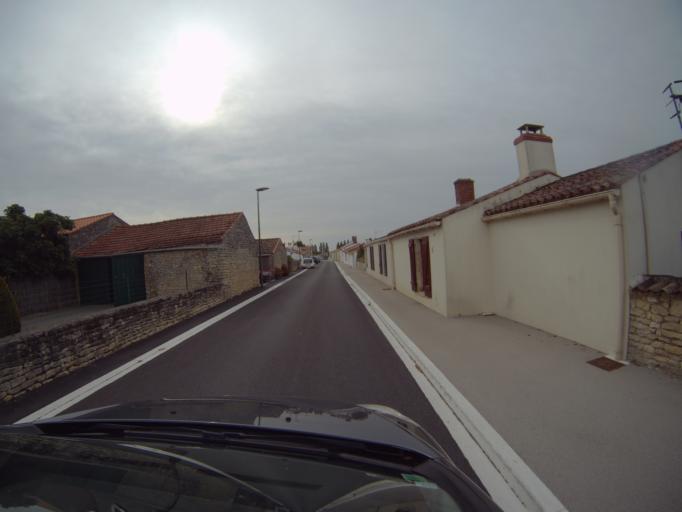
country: FR
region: Pays de la Loire
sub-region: Departement de la Vendee
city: Angles
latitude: 46.4063
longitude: -1.3832
